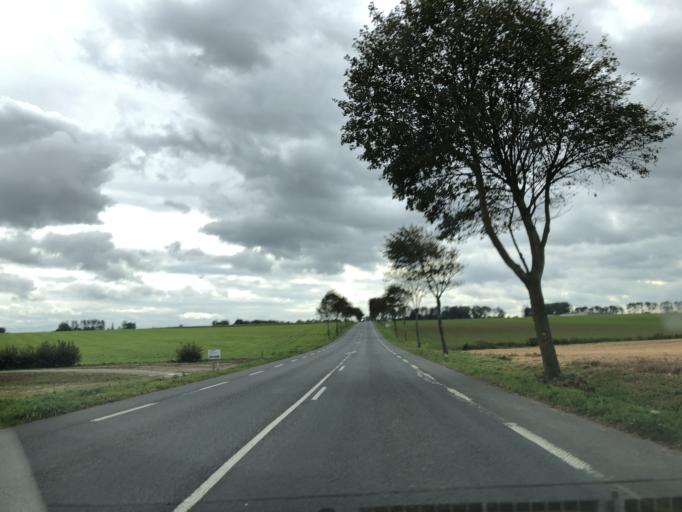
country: FR
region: Nord-Pas-de-Calais
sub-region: Departement du Pas-de-Calais
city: Fruges
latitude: 50.4929
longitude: 2.1277
